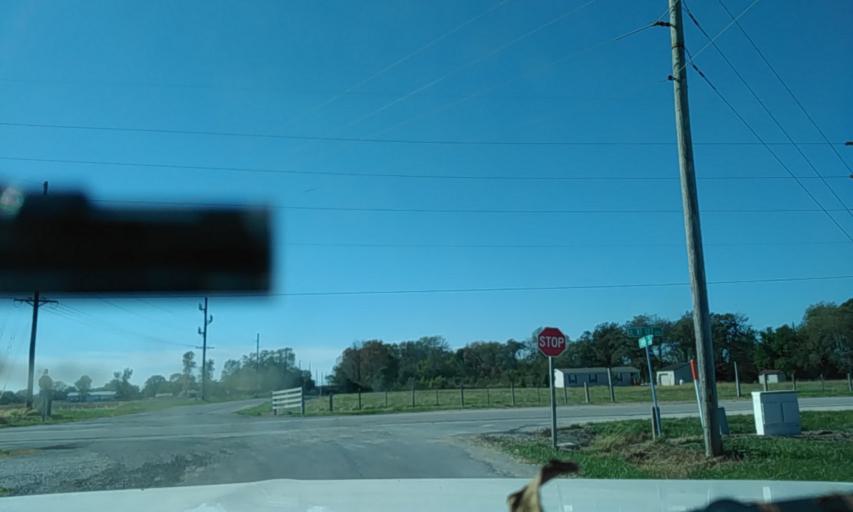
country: US
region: Illinois
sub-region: Bond County
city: Greenville
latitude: 38.9815
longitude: -89.4704
